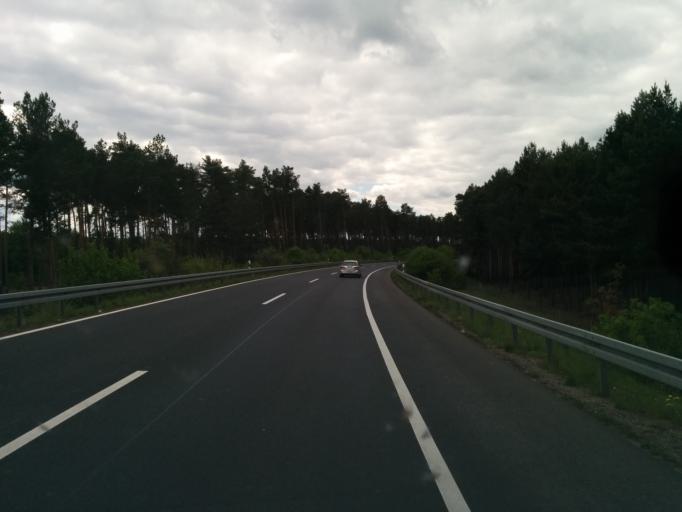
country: DE
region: Brandenburg
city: Gross Kreutz
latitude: 52.3418
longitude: 12.8150
